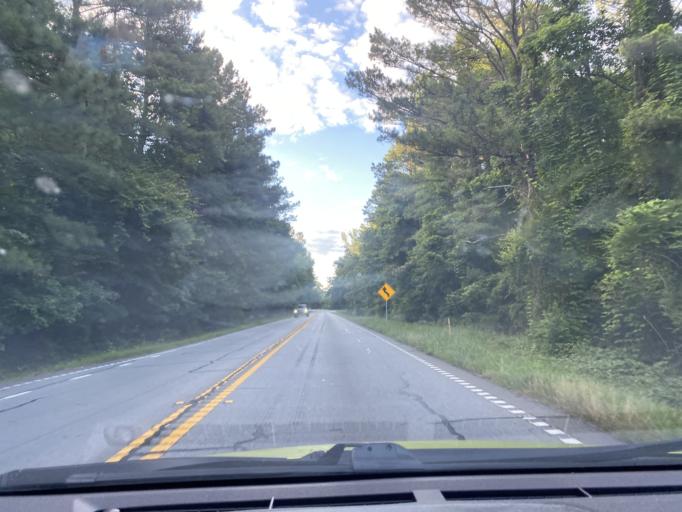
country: US
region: Georgia
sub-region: Fayette County
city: Peachtree City
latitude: 33.4177
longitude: -84.6824
